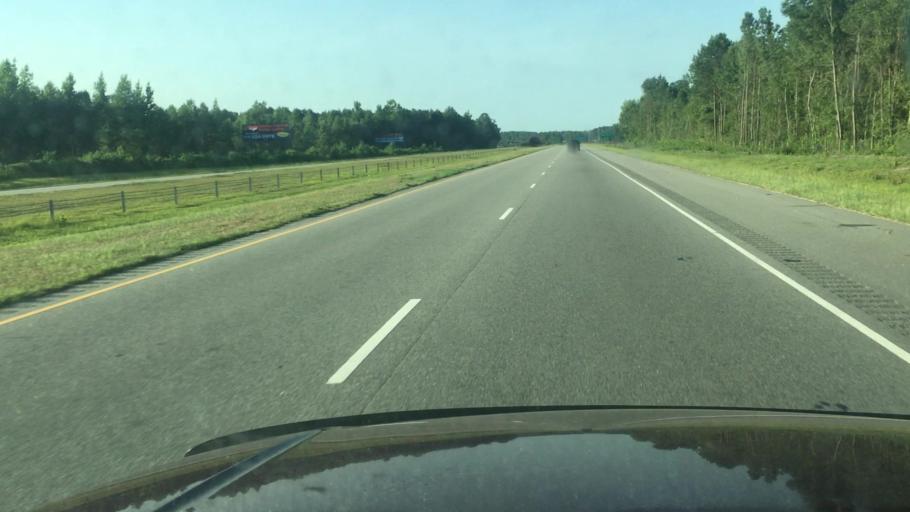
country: US
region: North Carolina
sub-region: Cumberland County
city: Fayetteville
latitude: 35.0234
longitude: -78.8723
